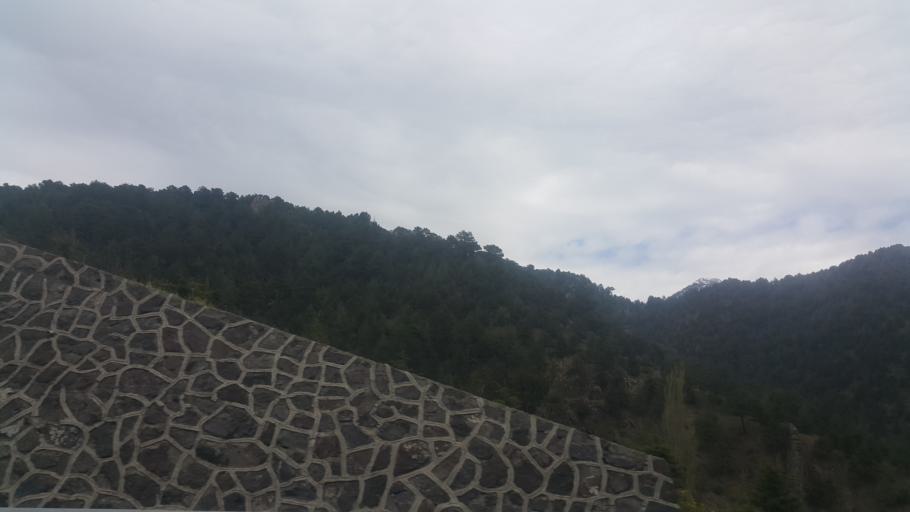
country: TR
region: Nigde
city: Ciftehan
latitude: 37.5151
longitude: 34.8177
